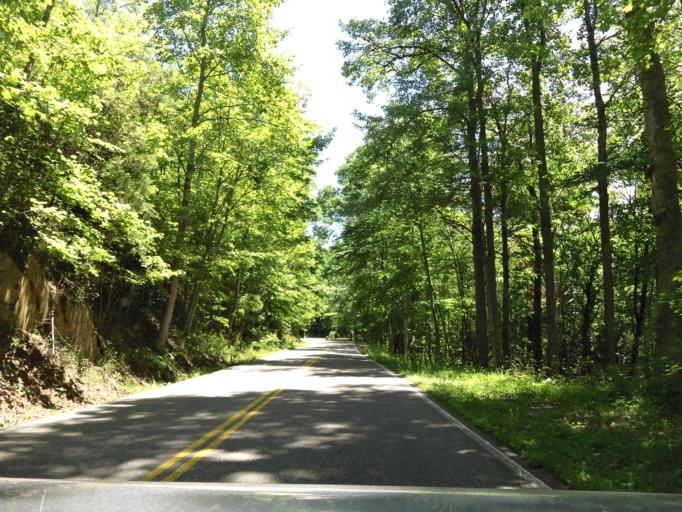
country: US
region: North Carolina
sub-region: Graham County
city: Robbinsville
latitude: 35.4771
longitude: -83.9222
